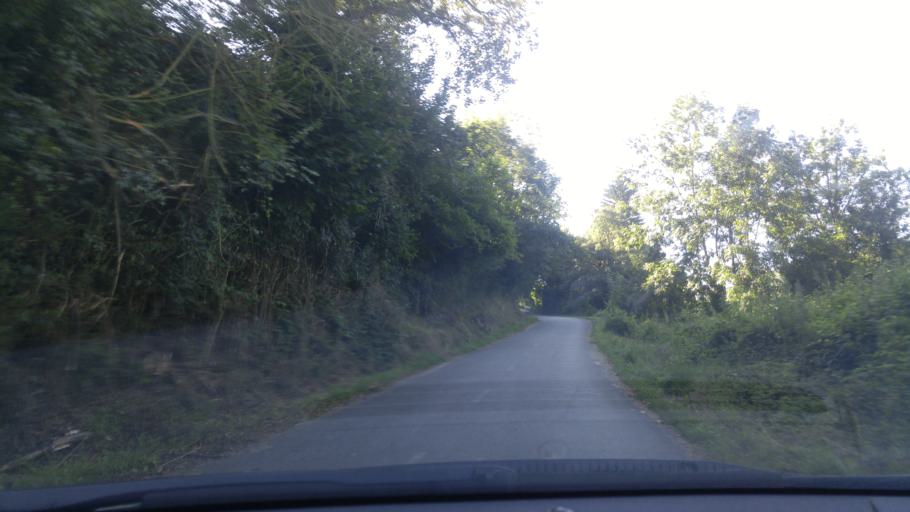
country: ES
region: Asturias
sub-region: Province of Asturias
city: Barzana
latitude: 43.1692
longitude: -5.9847
